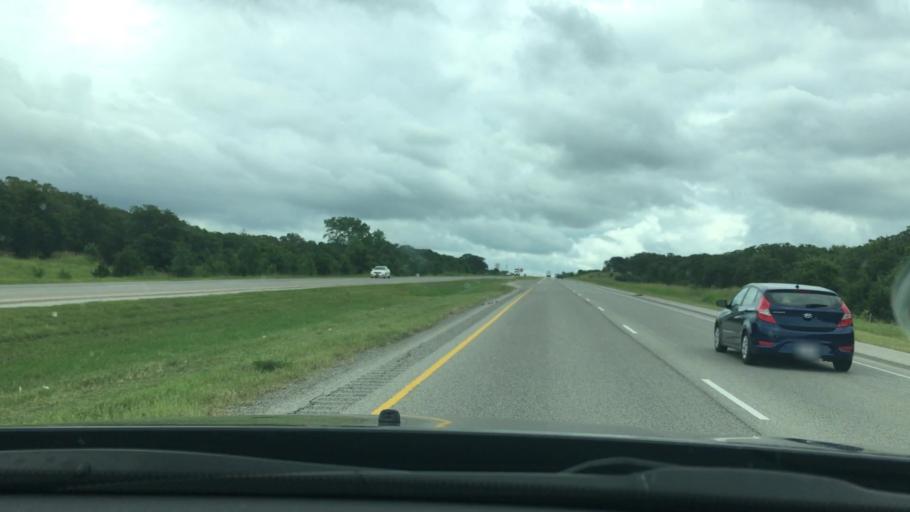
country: US
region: Oklahoma
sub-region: Carter County
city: Ardmore
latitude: 34.1305
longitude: -97.0839
